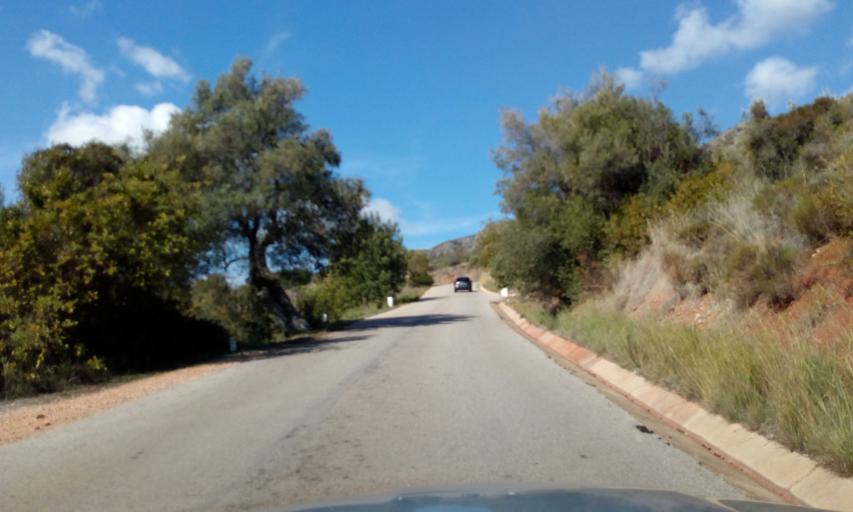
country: PT
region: Faro
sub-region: Loule
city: Boliqueime
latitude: 37.2500
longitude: -8.0947
